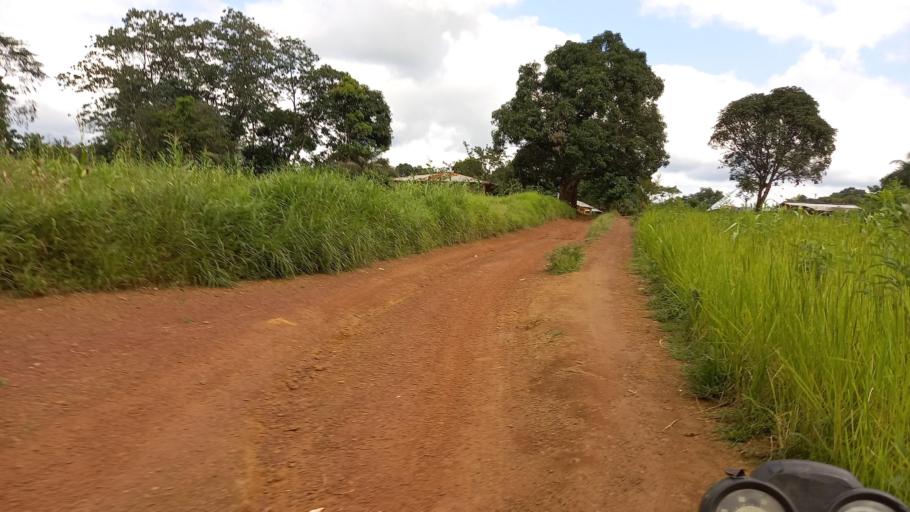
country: SL
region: Northern Province
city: Kamakwie
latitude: 9.5029
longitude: -12.2383
